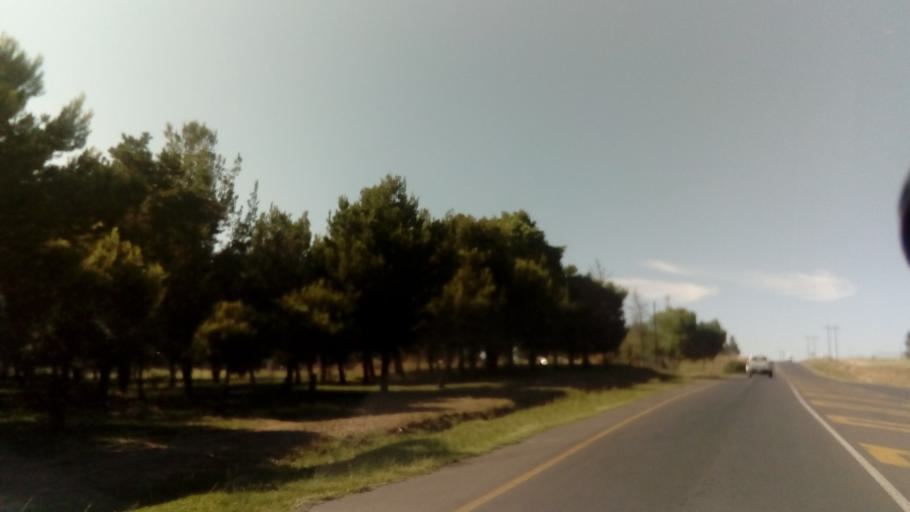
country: LS
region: Maseru
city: Maseru
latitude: -29.2387
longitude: 27.6070
